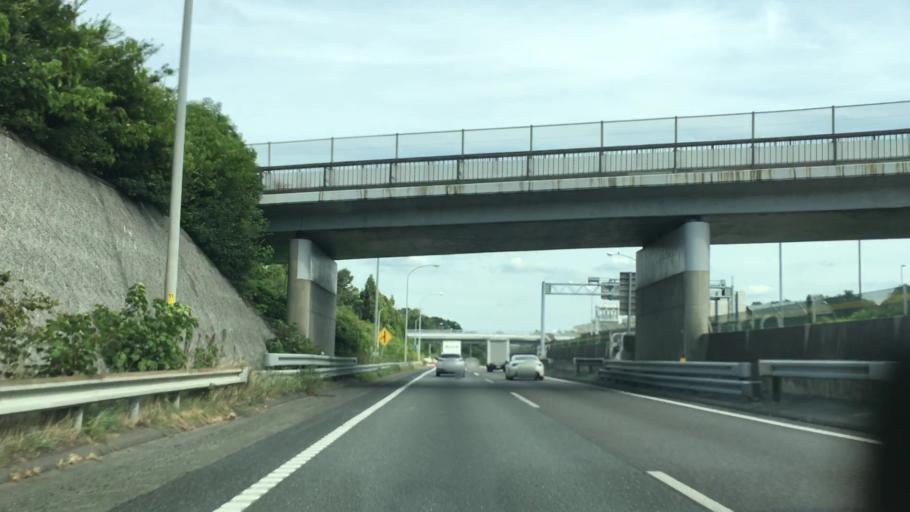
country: JP
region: Shiga Prefecture
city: Otsu-shi
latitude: 34.9965
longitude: 135.8699
